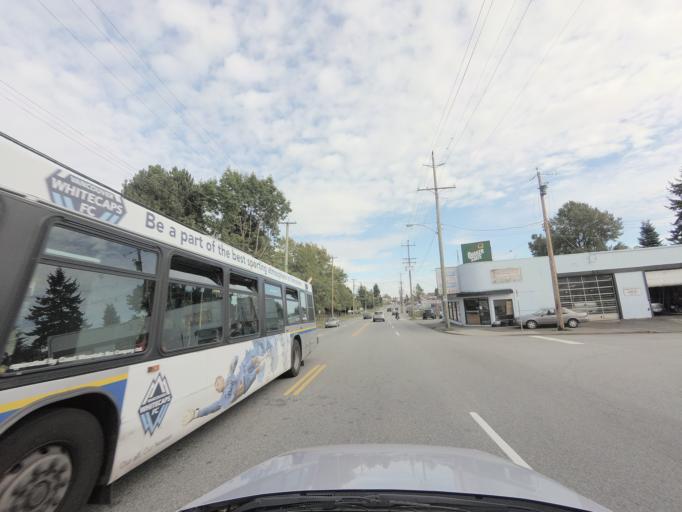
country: CA
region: British Columbia
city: New Westminster
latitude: 49.2147
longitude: -122.9398
